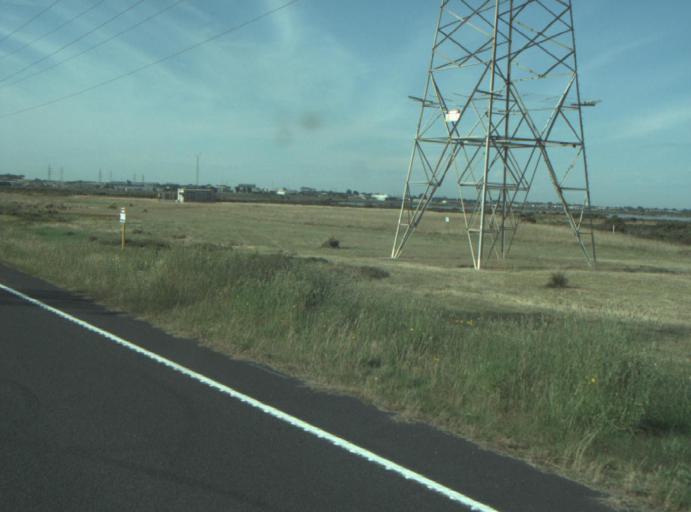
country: AU
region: Victoria
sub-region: Greater Geelong
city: East Geelong
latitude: -38.1432
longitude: 144.4285
